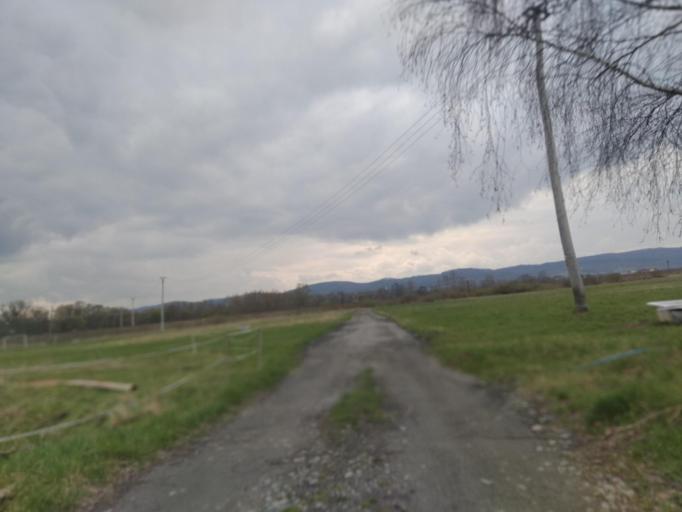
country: PL
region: Subcarpathian Voivodeship
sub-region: Powiat strzyzowski
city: Wysoka Strzyzowska
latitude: 49.8773
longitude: 21.7187
